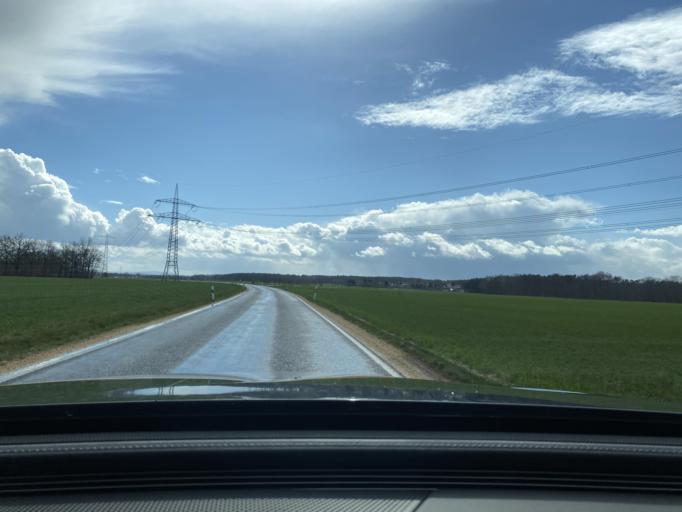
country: DE
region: Saxony
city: Grossdubrau
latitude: 51.2953
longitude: 14.4473
